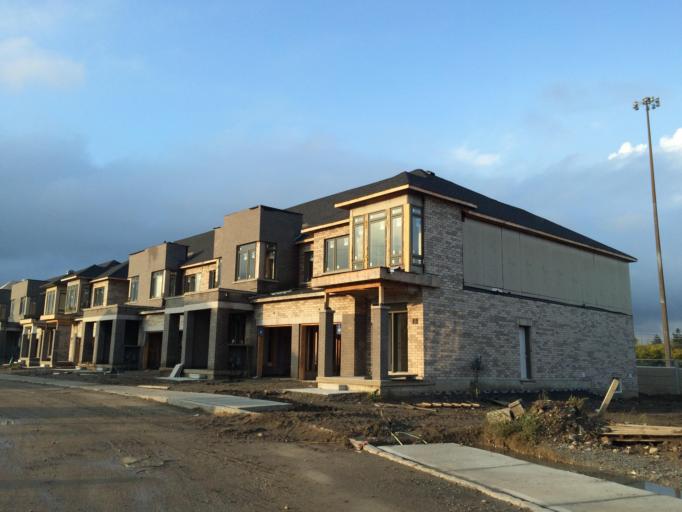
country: CA
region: Ontario
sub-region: Wellington County
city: Guelph
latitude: 43.5271
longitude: -80.2680
